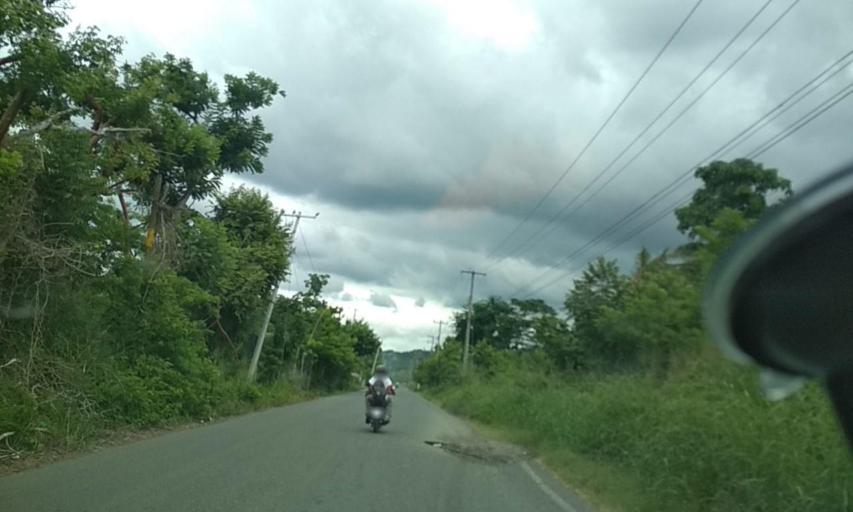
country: MX
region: Veracruz
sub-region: Papantla
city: Residencial Tajin
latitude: 20.6334
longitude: -97.3755
